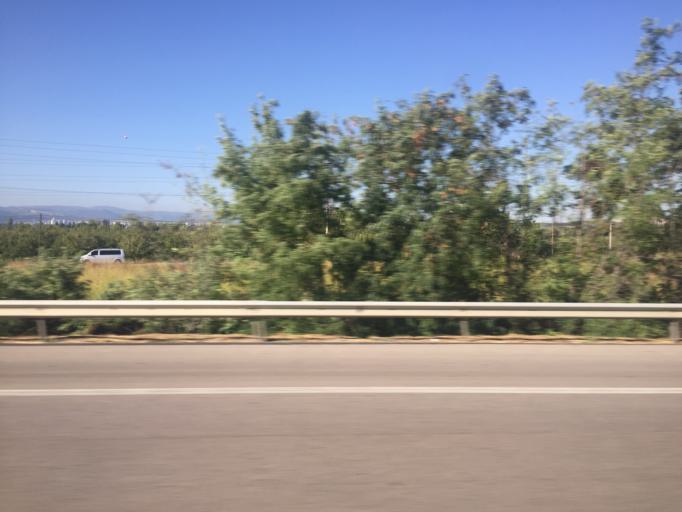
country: TR
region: Bursa
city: Demirtas
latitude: 40.2749
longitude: 29.0467
